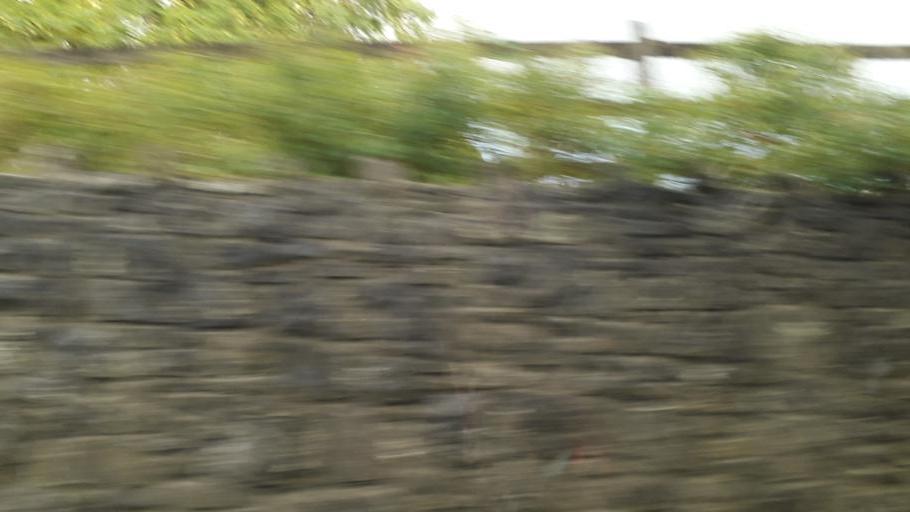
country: IE
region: Leinster
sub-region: An Longfort
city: Lanesborough
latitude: 53.7709
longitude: -8.1030
